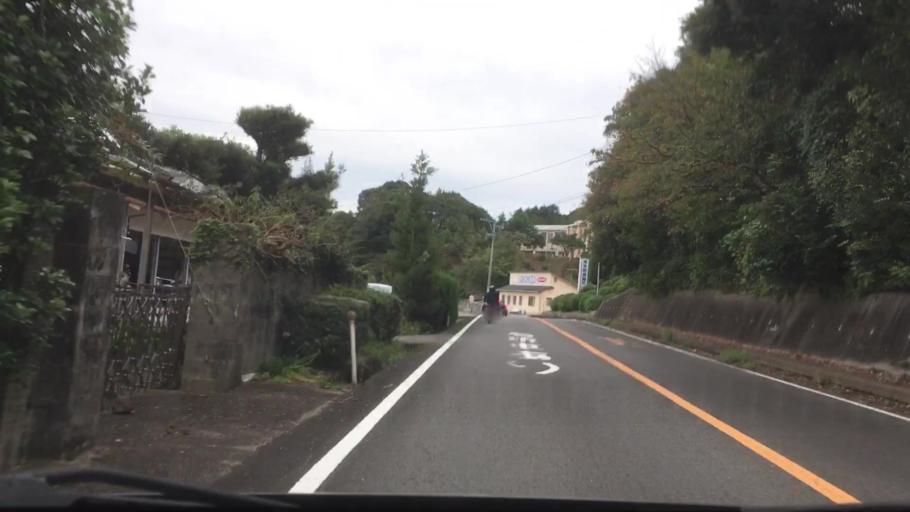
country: JP
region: Nagasaki
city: Sasebo
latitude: 33.0157
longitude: 129.7329
